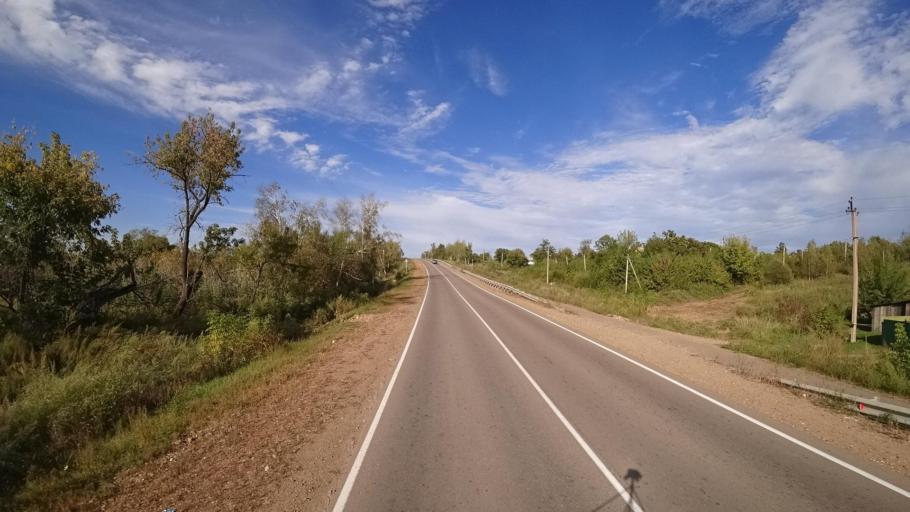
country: RU
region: Primorskiy
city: Dostoyevka
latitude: 44.2970
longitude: 133.4451
